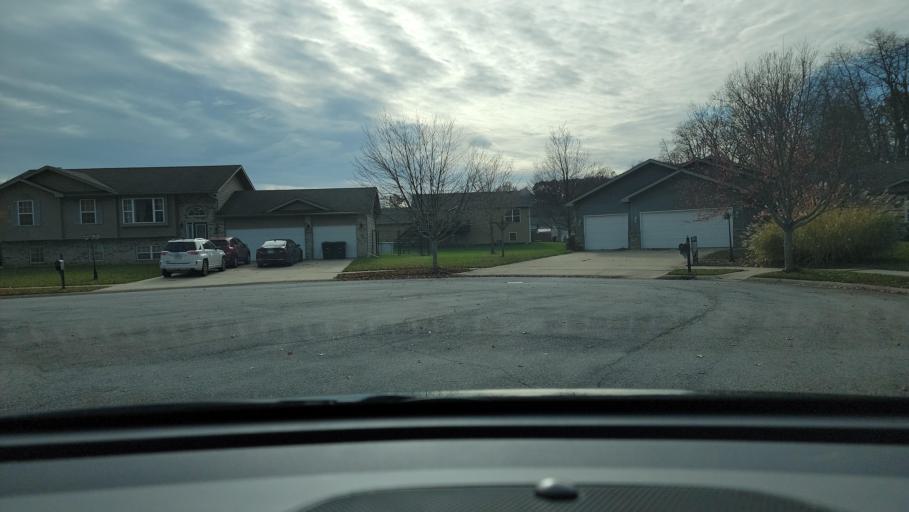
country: US
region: Indiana
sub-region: Porter County
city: South Haven
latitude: 41.5833
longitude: -87.1289
